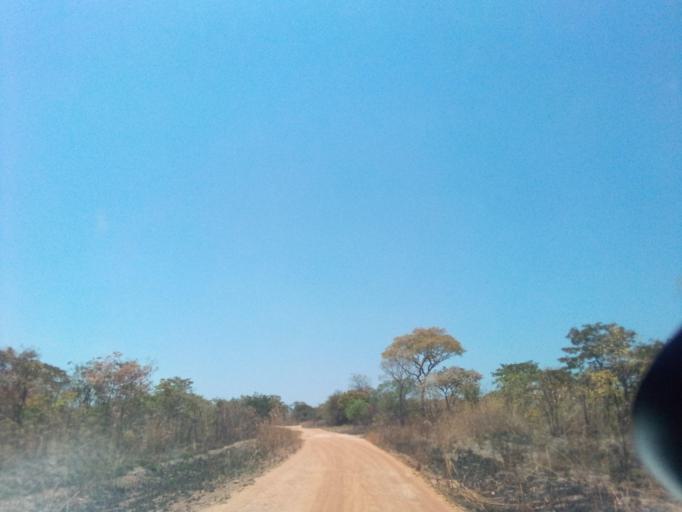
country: ZM
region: Northern
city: Mpika
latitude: -12.2535
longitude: 30.6787
